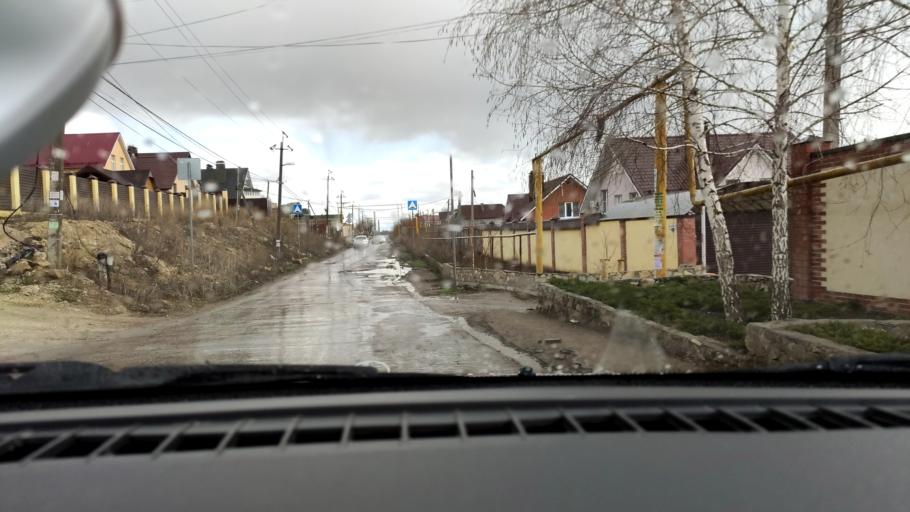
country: RU
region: Samara
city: Novosemeykino
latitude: 53.3288
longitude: 50.2895
